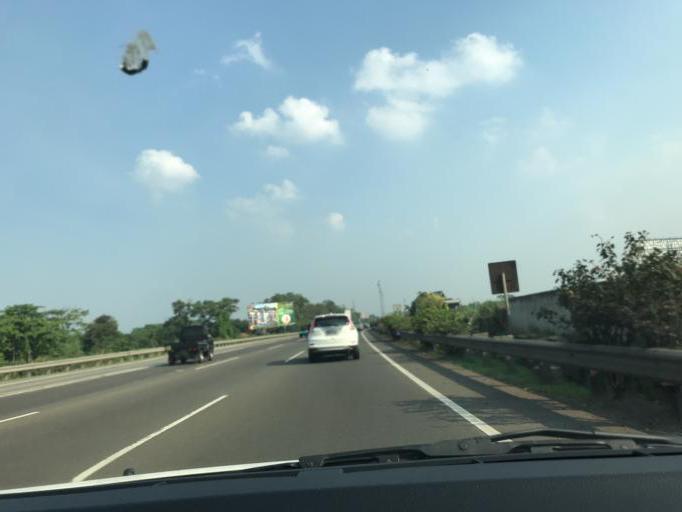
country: ID
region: West Java
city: Cileungsir
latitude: -6.4064
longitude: 106.8985
